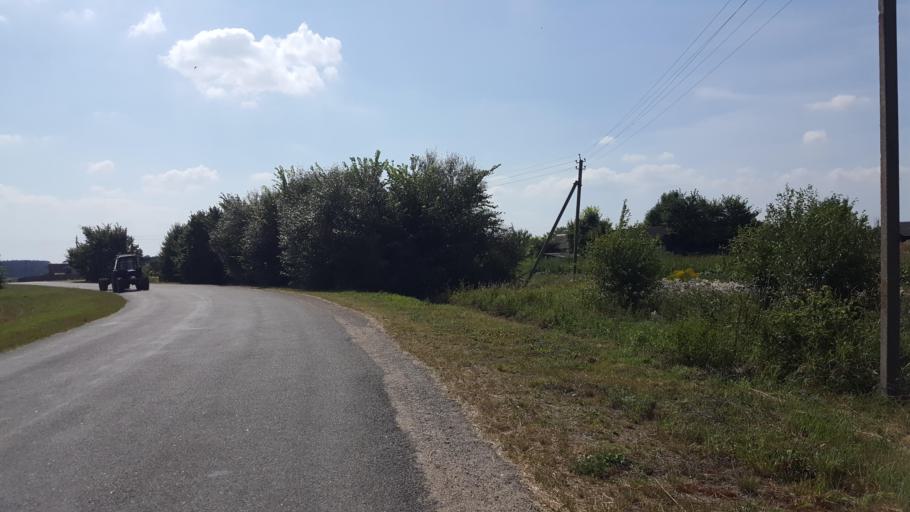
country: PL
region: Podlasie
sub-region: Powiat hajnowski
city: Czeremcha
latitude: 52.5381
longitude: 23.5360
